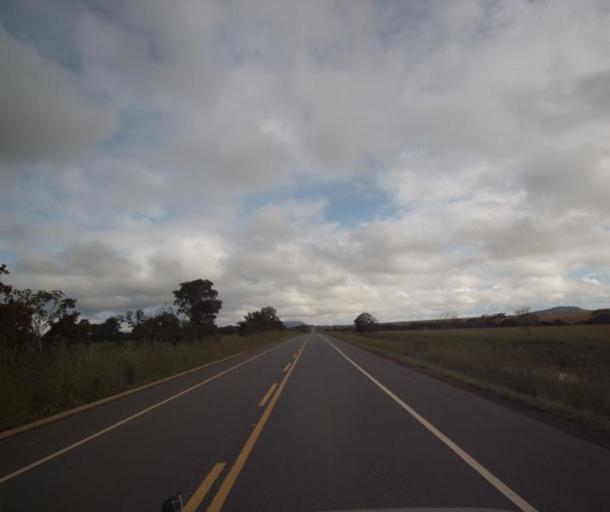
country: BR
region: Goias
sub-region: Padre Bernardo
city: Padre Bernardo
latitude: -15.3063
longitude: -48.6672
